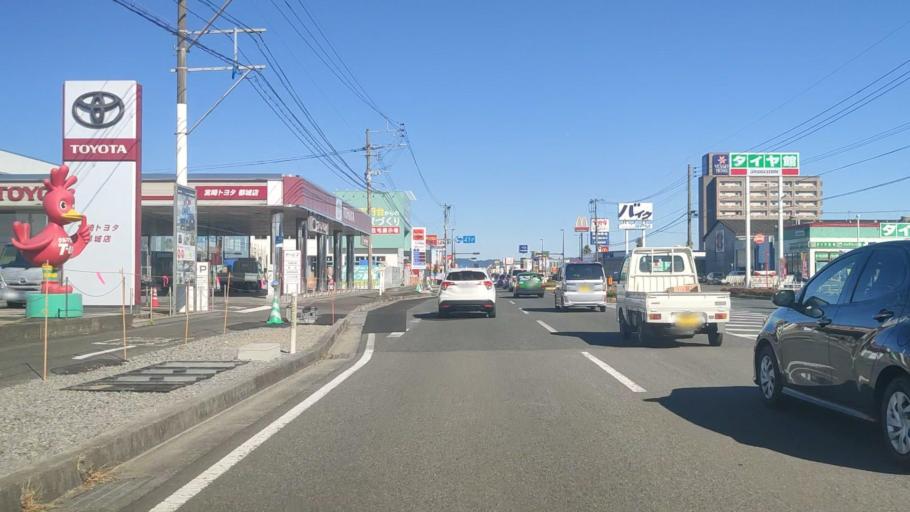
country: JP
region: Miyazaki
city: Miyakonojo
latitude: 31.7570
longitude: 131.0833
